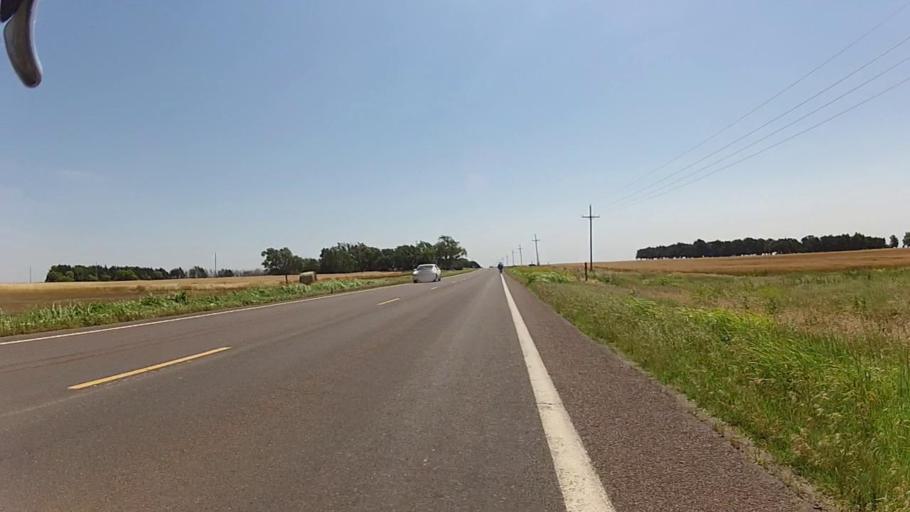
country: US
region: Kansas
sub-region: Sumner County
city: Caldwell
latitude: 37.0327
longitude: -97.5662
